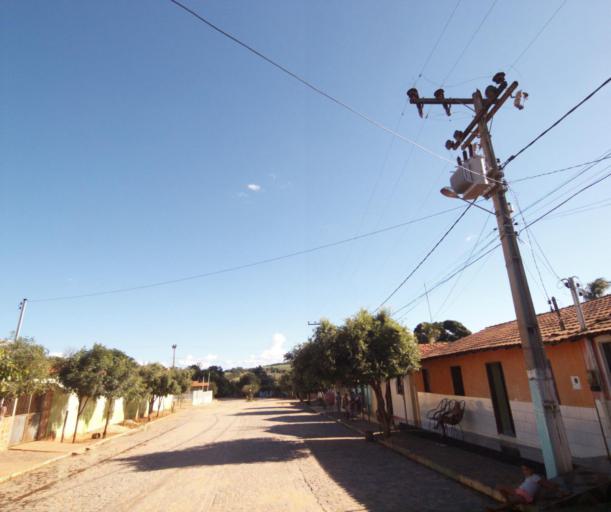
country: BR
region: Bahia
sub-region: Carinhanha
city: Carinhanha
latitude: -14.2604
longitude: -44.5259
